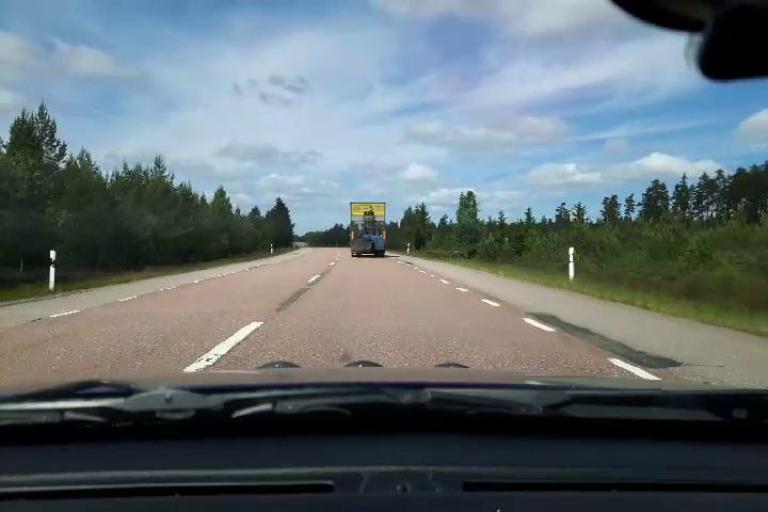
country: SE
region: Uppsala
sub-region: Osthammars Kommun
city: Bjorklinge
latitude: 60.1702
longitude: 17.4891
